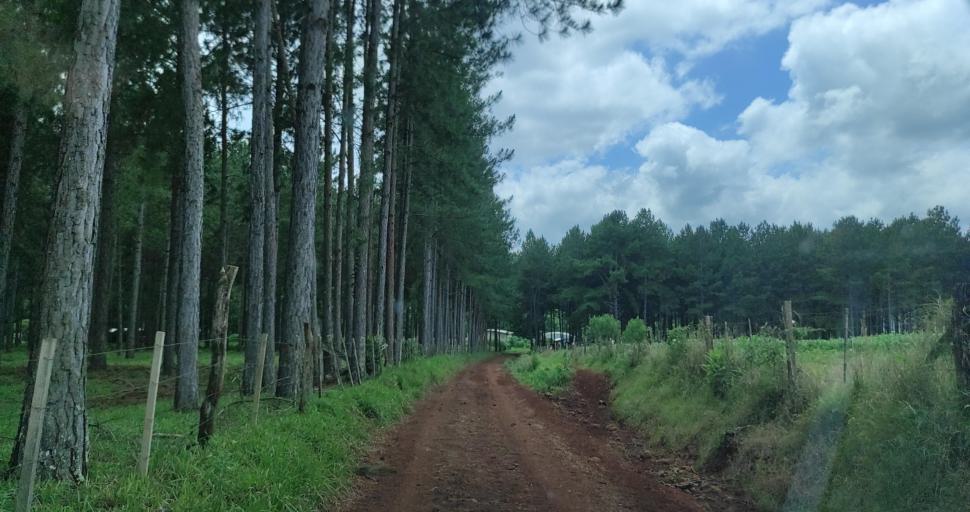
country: AR
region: Misiones
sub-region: Departamento de Veinticinco de Mayo
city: Veinticinco de Mayo
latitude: -27.4197
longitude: -54.7049
